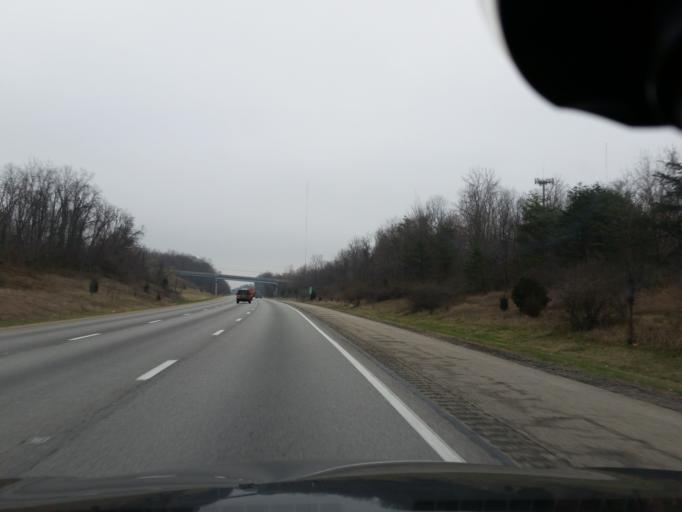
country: US
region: Pennsylvania
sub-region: Cumberland County
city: Enola
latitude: 40.3037
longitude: -76.9608
